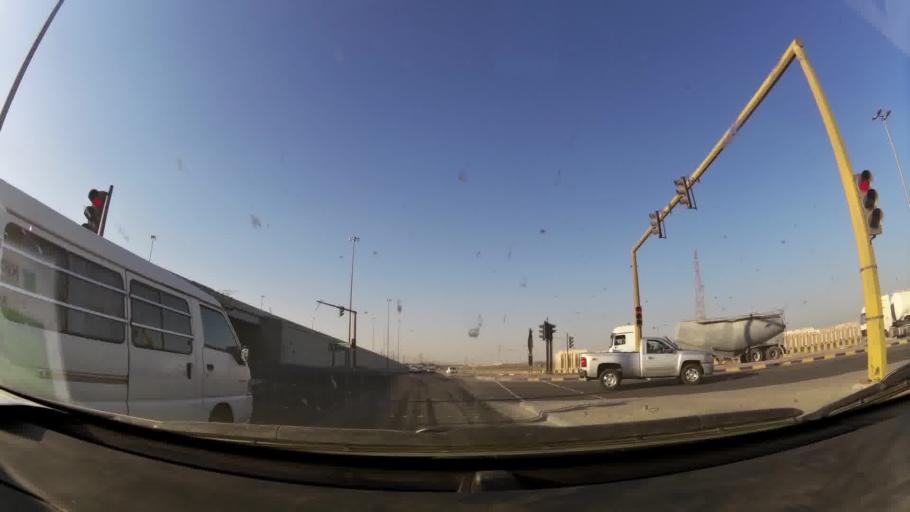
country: KW
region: Al Ahmadi
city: Al Fahahil
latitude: 29.0367
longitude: 48.1192
